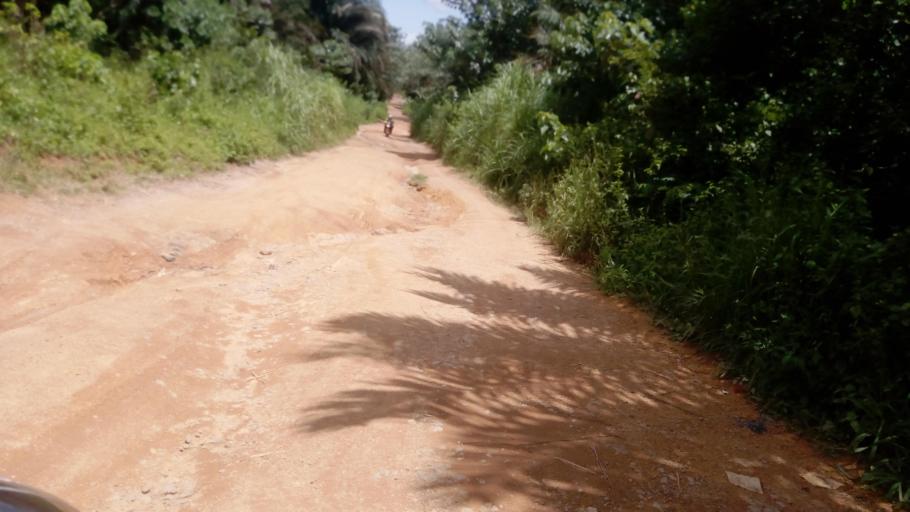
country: SL
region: Northern Province
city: Binkolo
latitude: 8.9536
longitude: -11.9740
